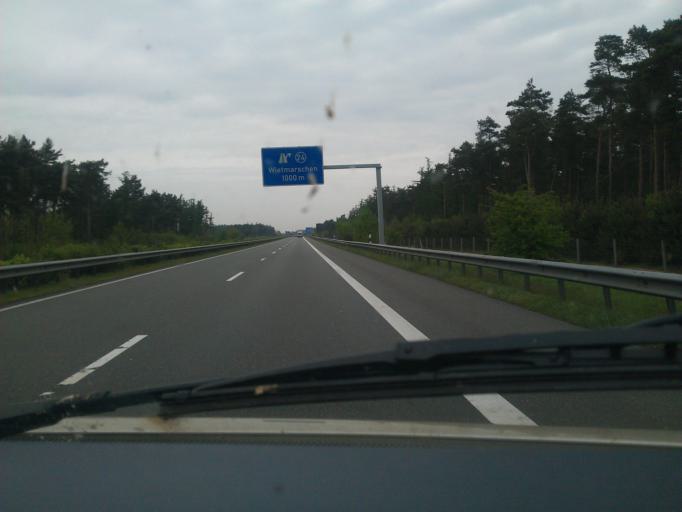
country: DE
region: Lower Saxony
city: Wietmarschen
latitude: 52.5330
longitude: 7.1972
